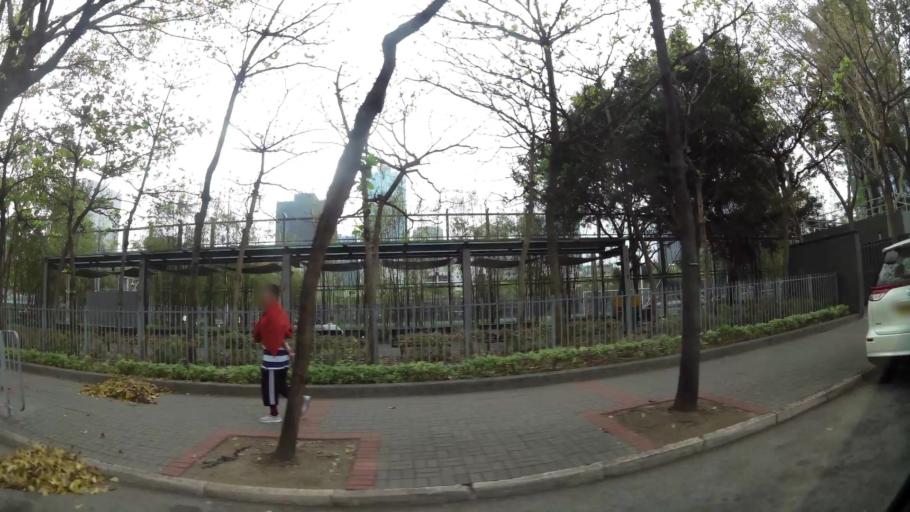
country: HK
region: Kowloon City
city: Kowloon
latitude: 22.3276
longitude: 114.2080
